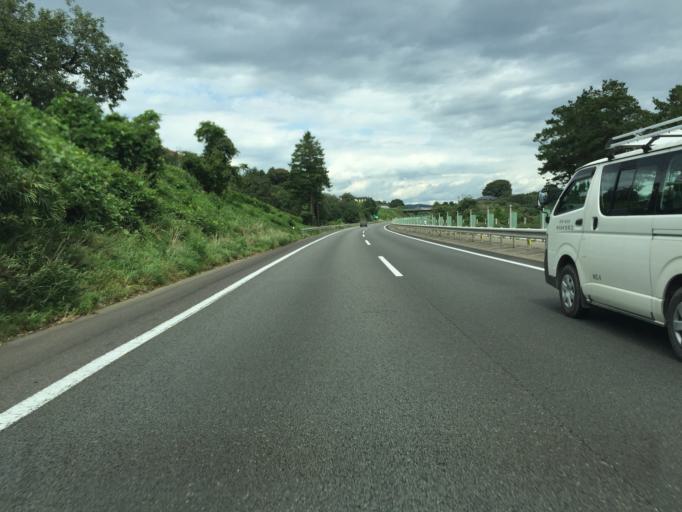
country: JP
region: Miyagi
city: Shiroishi
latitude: 38.0590
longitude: 140.6532
